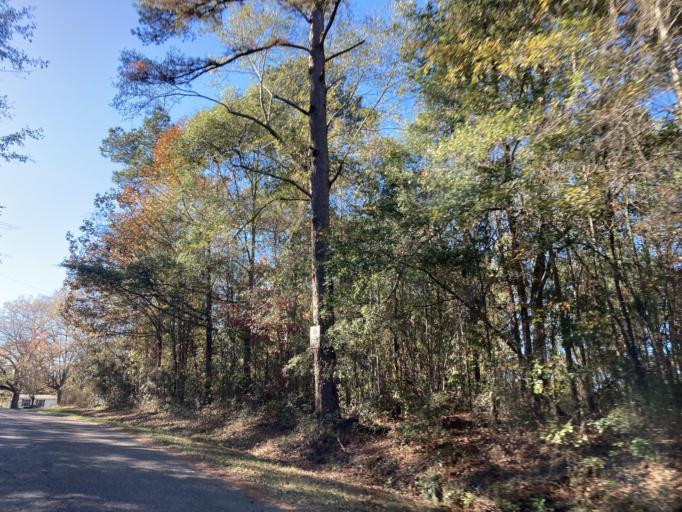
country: US
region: Mississippi
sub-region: Lamar County
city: Sumrall
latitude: 31.3028
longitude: -89.6389
